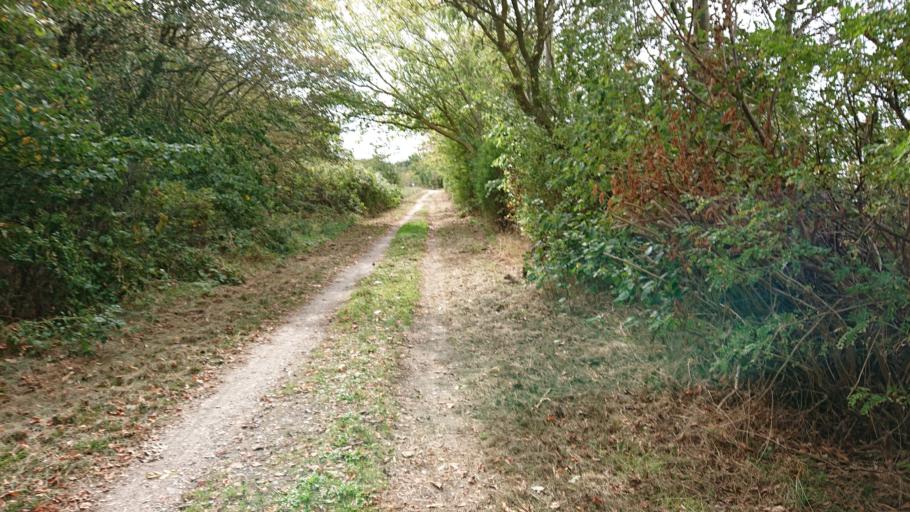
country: DE
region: Mecklenburg-Vorpommern
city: Altefahr
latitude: 54.3396
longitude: 13.1148
